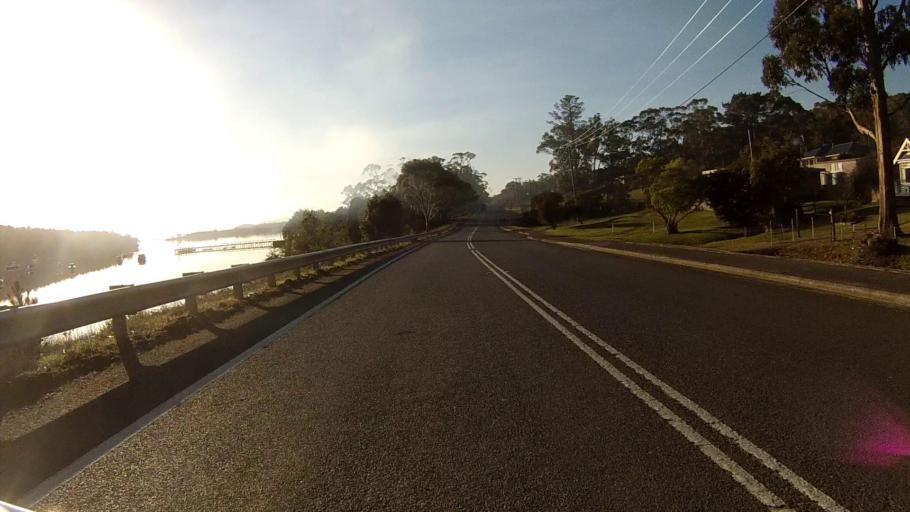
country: AU
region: Tasmania
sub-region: Clarence
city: Sandford
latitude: -43.0517
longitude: 147.8650
